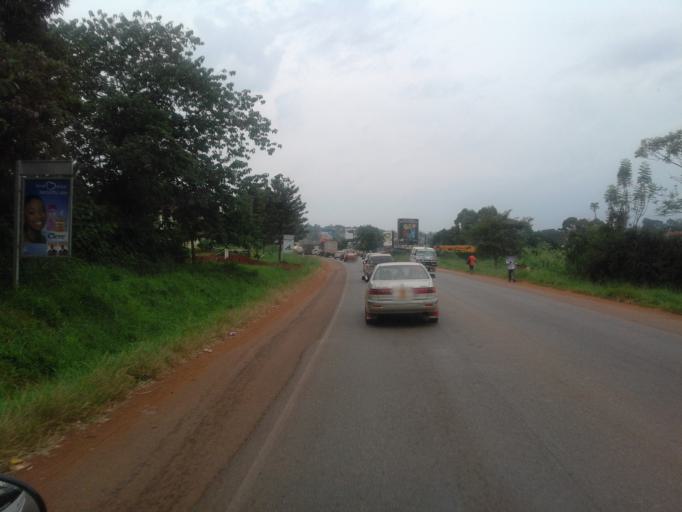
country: UG
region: Eastern Region
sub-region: Jinja District
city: Jinja
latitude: 0.4443
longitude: 33.1952
